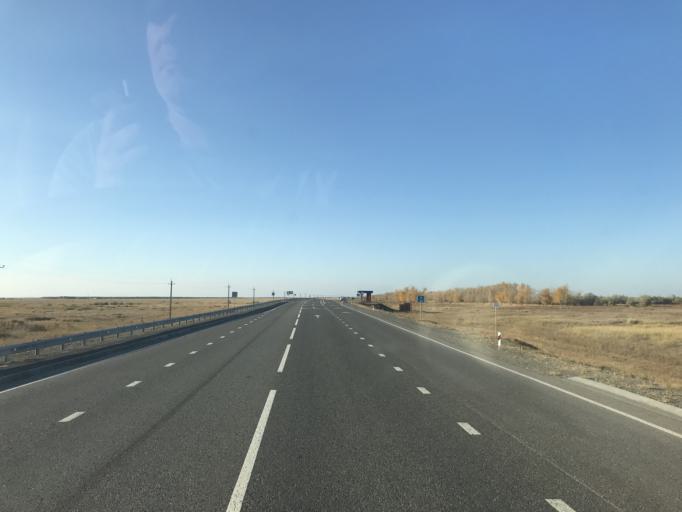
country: KZ
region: Pavlodar
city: Koktobe
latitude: 51.9271
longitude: 77.3333
